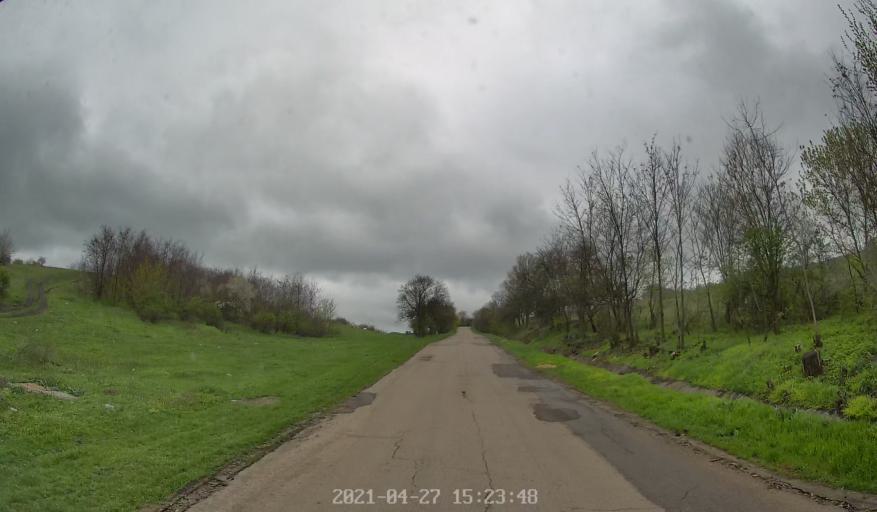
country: MD
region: Chisinau
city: Vadul lui Voda
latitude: 47.0186
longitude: 29.0248
